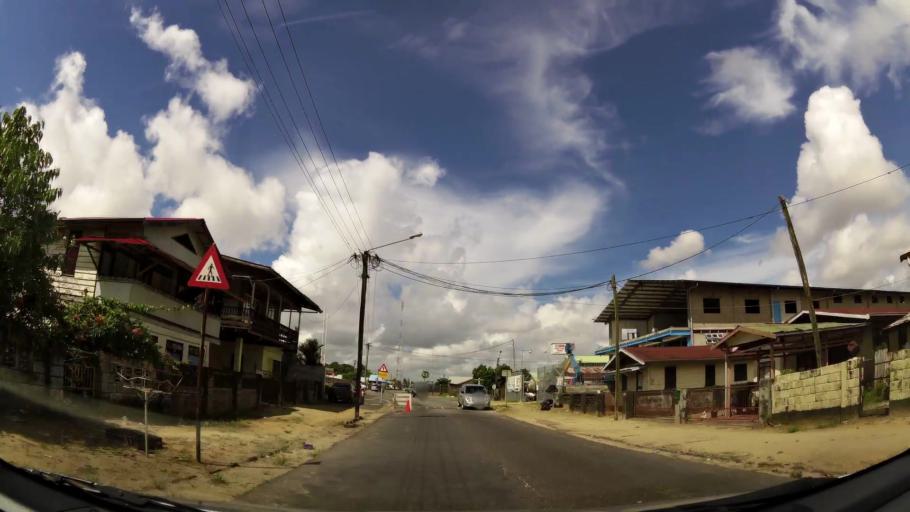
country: SR
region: Paramaribo
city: Paramaribo
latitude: 5.8278
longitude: -55.1756
